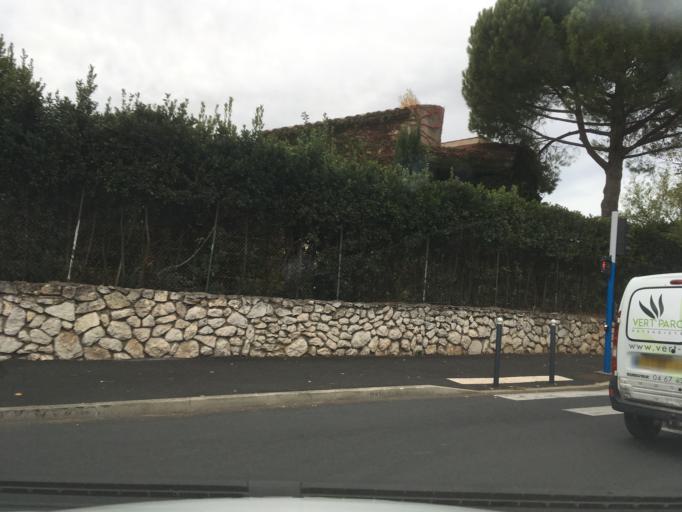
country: FR
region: Languedoc-Roussillon
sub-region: Departement de l'Herault
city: Castelnau-le-Lez
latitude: 43.6311
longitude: 3.8852
